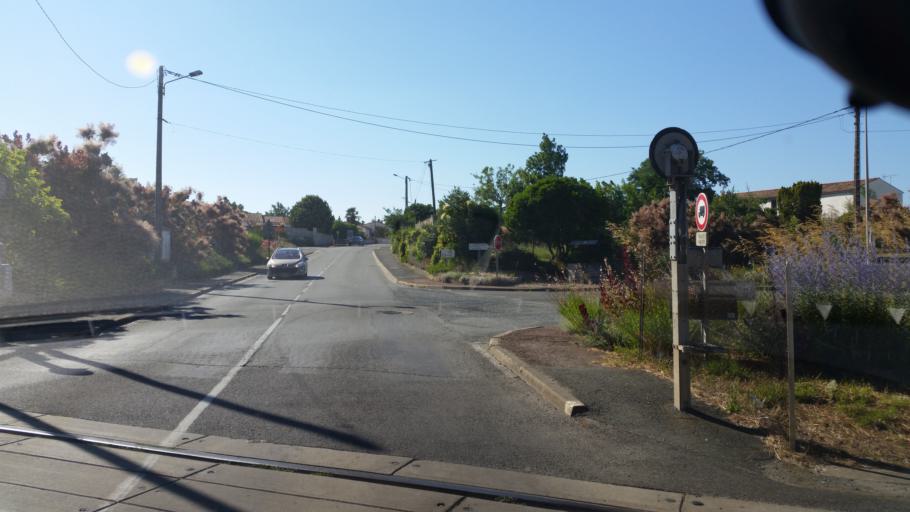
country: FR
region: Poitou-Charentes
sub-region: Departement de la Charente-Maritime
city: Marans
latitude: 46.3035
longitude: -0.9855
